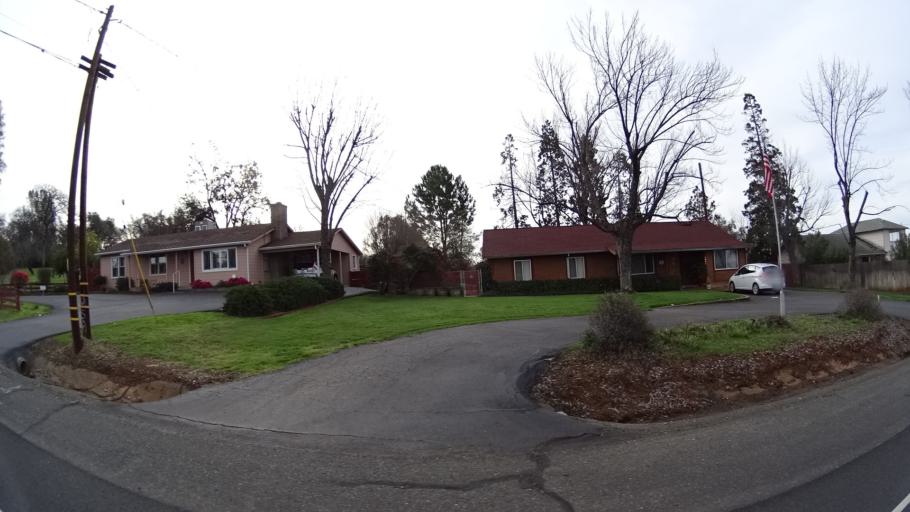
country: US
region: California
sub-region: Butte County
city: Oroville East
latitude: 39.5105
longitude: -121.4875
